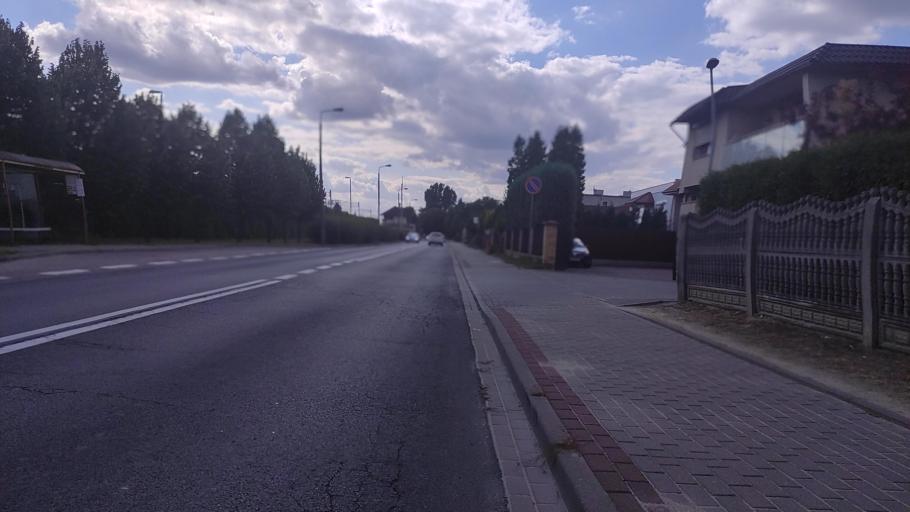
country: PL
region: Greater Poland Voivodeship
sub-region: Powiat poznanski
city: Swarzedz
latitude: 52.4050
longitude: 17.0815
